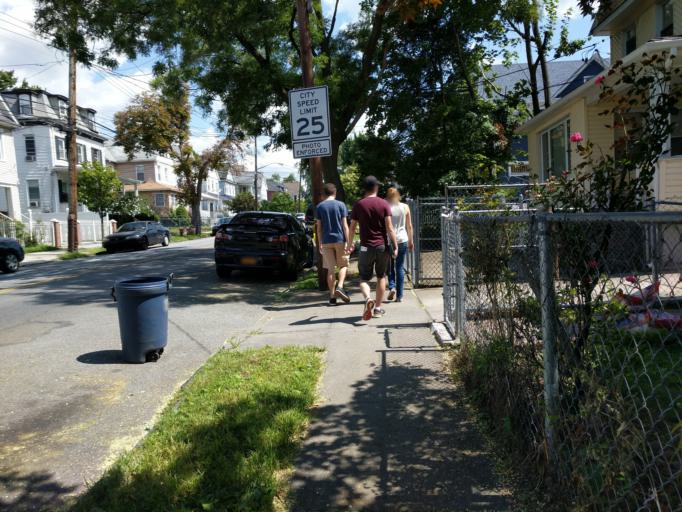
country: US
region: New Jersey
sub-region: Hudson County
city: Bayonne
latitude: 40.6327
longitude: -74.1163
